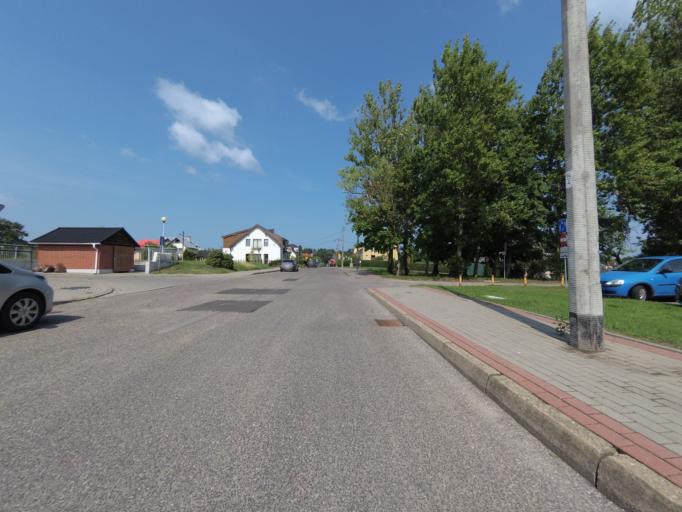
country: PL
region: Pomeranian Voivodeship
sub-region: Gdynia
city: Gdynia
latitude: 54.4920
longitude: 18.5144
